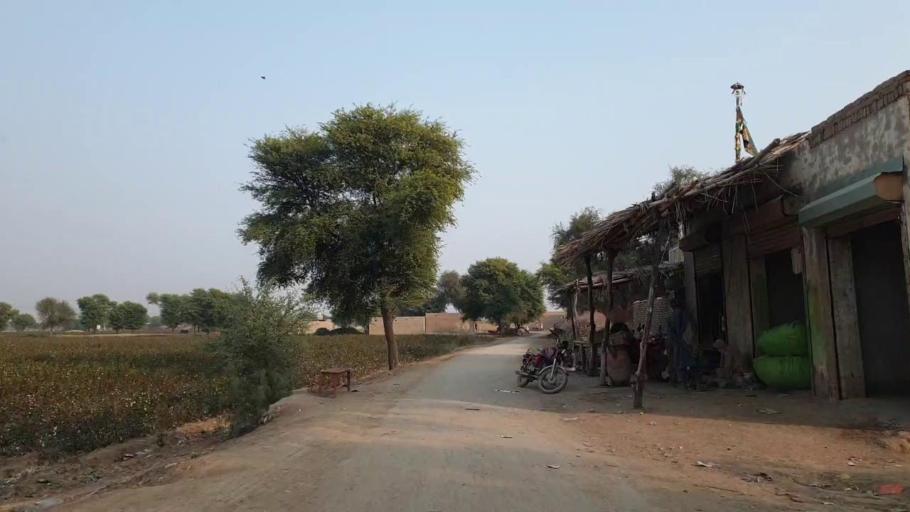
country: PK
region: Sindh
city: Bhan
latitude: 26.4955
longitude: 67.7479
